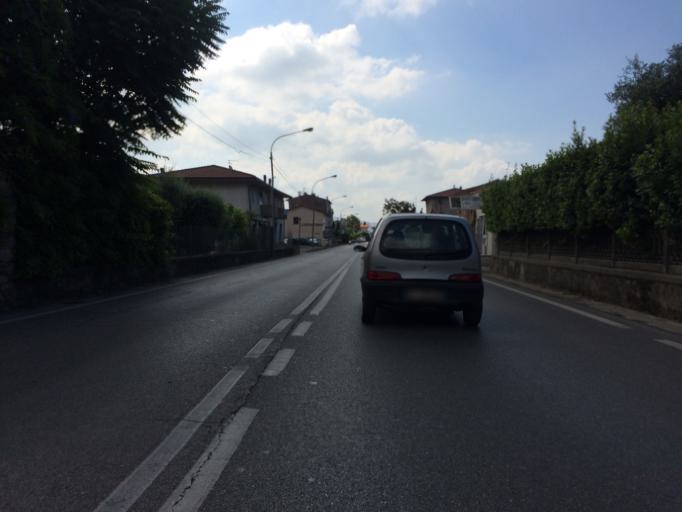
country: IT
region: Tuscany
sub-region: Provincia di Lucca
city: Ripa-Pozzi-Querceta-Ponterosso
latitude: 43.9708
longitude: 10.2081
